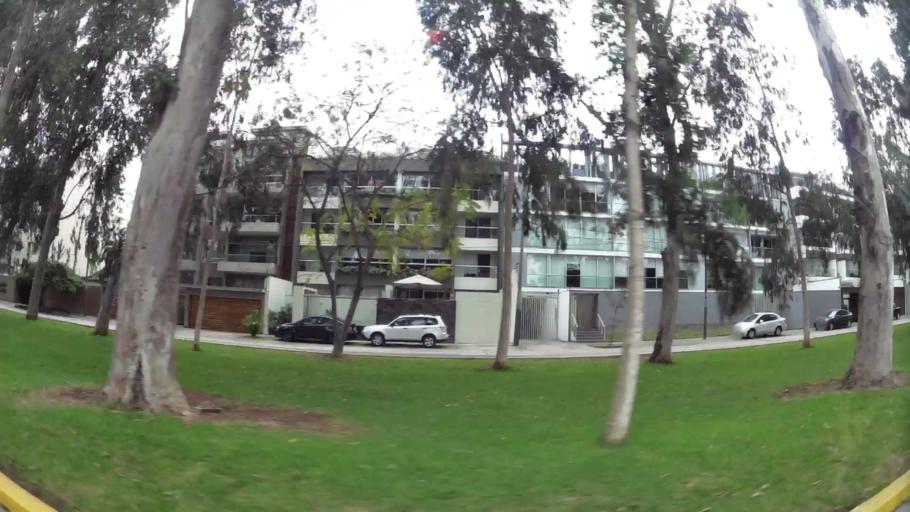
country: PE
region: Lima
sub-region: Lima
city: San Luis
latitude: -12.1055
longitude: -76.9828
